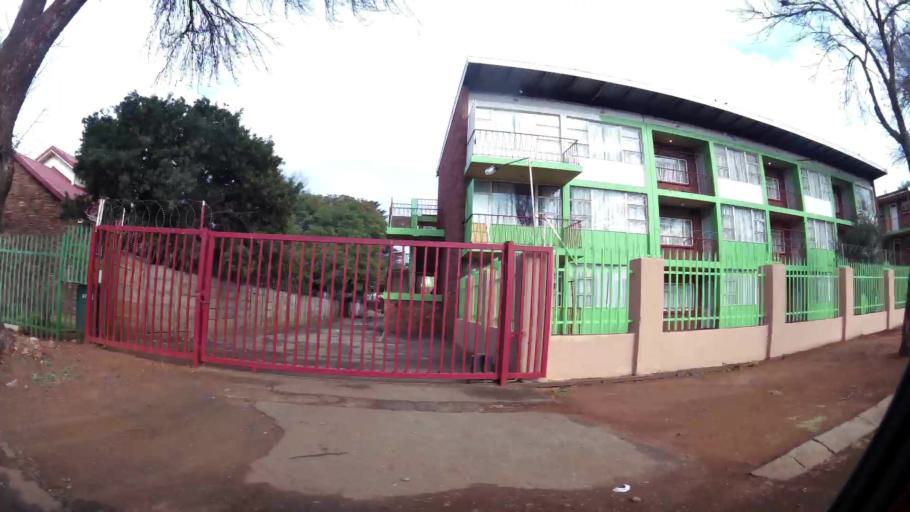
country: ZA
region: Gauteng
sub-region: Sedibeng District Municipality
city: Vanderbijlpark
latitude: -26.7021
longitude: 27.8274
